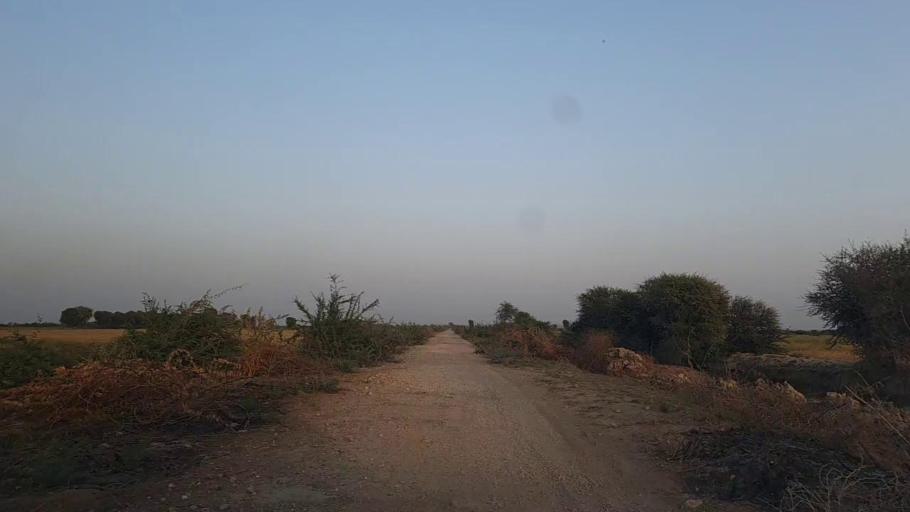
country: PK
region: Sindh
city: Naukot
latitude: 24.6957
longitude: 69.2749
